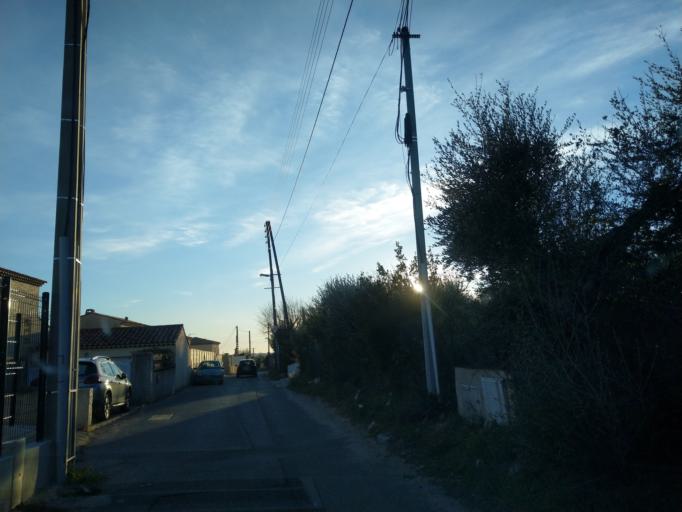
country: FR
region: Provence-Alpes-Cote d'Azur
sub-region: Departement des Bouches-du-Rhone
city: Plan-de-Cuques
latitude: 43.3496
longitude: 5.4552
